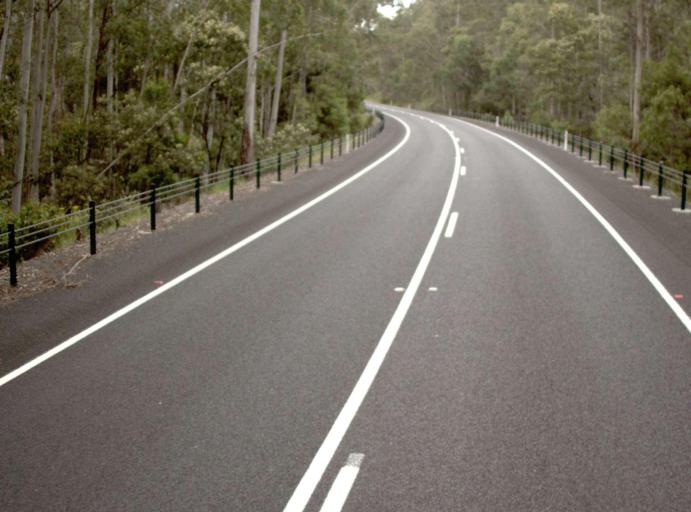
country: AU
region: New South Wales
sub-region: Bombala
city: Bombala
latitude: -37.3065
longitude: 149.2092
